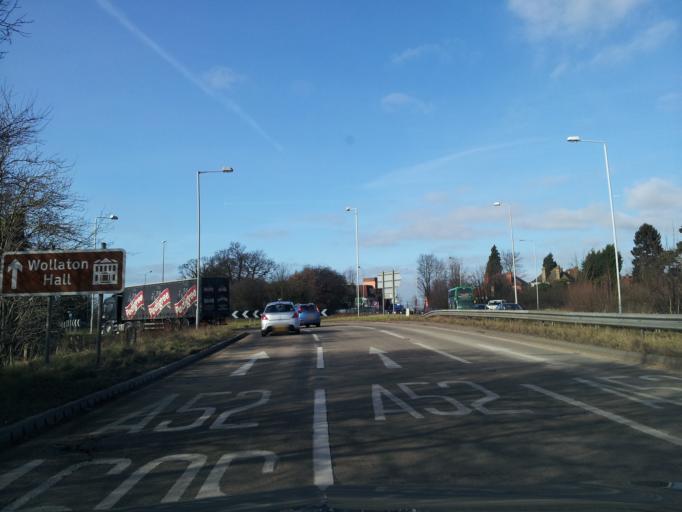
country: GB
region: England
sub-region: Nottinghamshire
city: Ruddington
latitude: 52.9070
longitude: -1.1431
